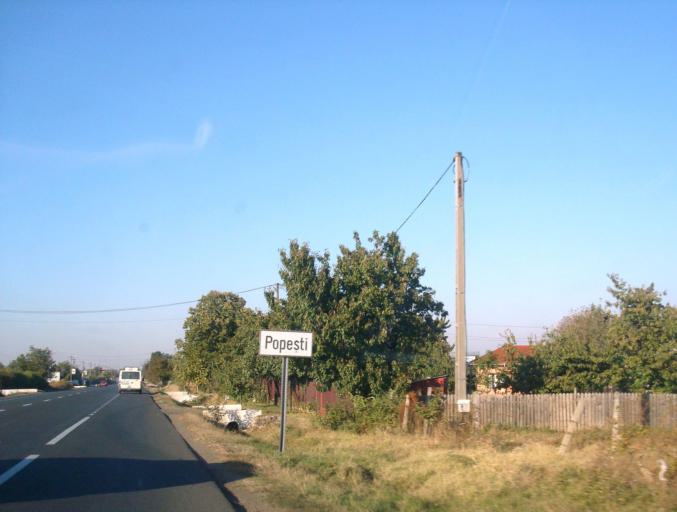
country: RO
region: Vrancea
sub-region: Comuna Popesti
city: Popesti
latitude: 45.5820
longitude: 27.0993
